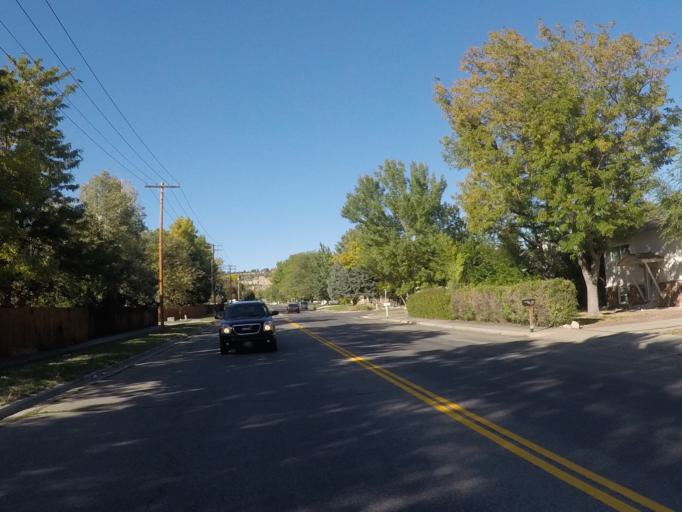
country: US
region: Montana
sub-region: Yellowstone County
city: Billings
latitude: 45.7871
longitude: -108.5903
